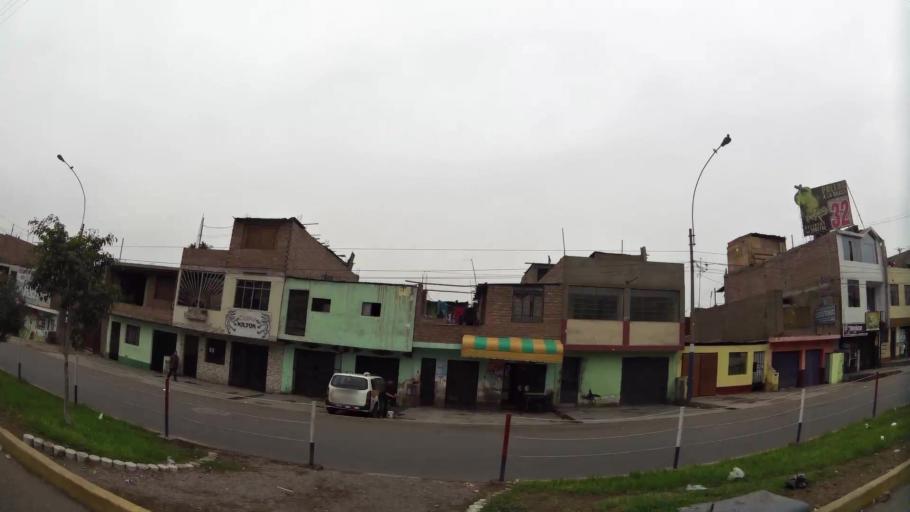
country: PE
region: Lima
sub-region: Lima
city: Independencia
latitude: -11.9665
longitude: -77.0094
